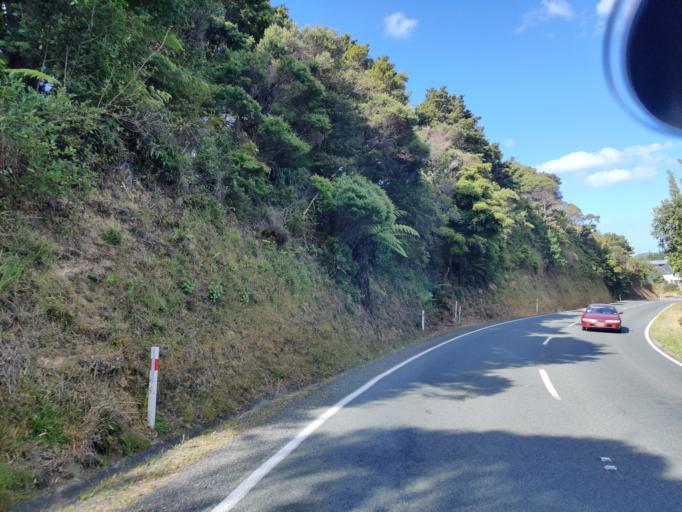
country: NZ
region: Northland
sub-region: Whangarei
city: Ngunguru
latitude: -35.6175
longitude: 174.5168
